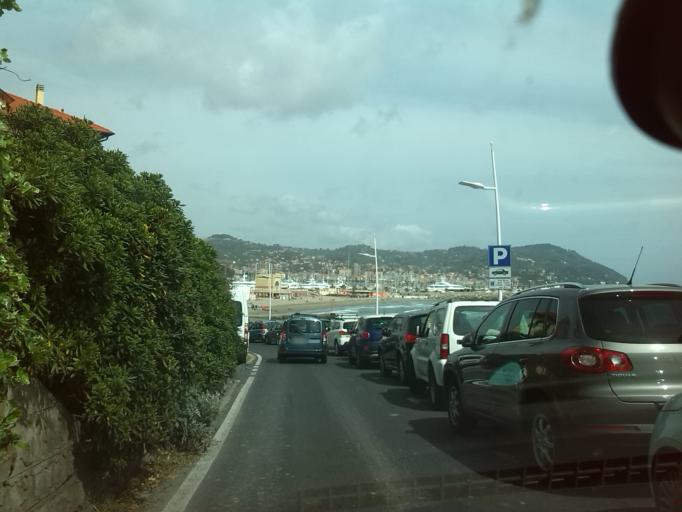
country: IT
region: Liguria
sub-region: Provincia di Imperia
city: Imperia
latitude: 43.8743
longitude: 8.0181
